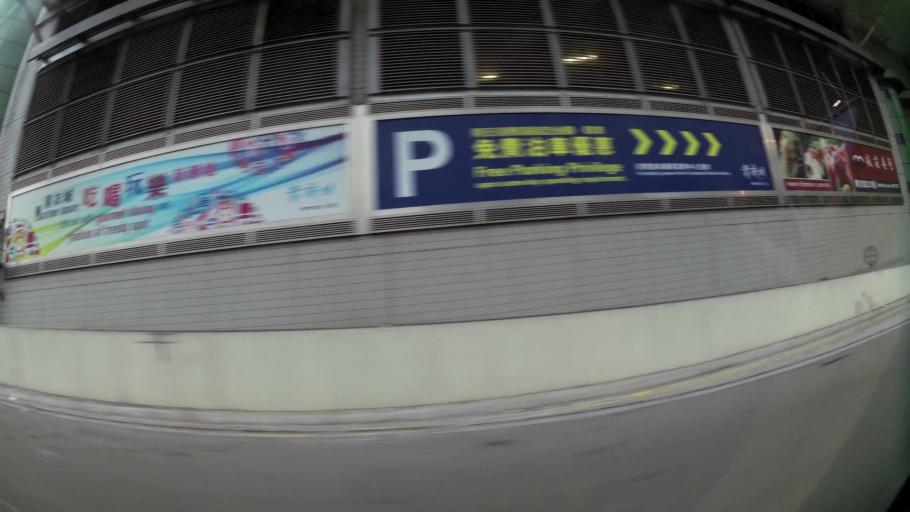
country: HK
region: Tsuen Wan
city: Tsuen Wan
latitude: 22.3595
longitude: 114.1080
